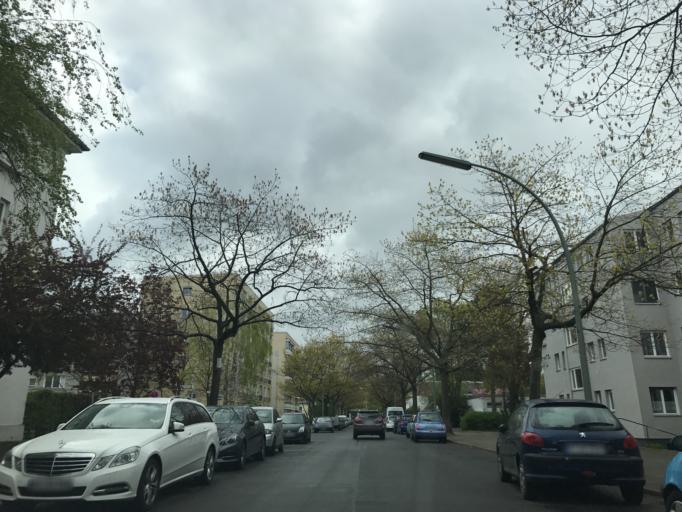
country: DE
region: Berlin
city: Charlottenburg-Nord
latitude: 52.5382
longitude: 13.2838
